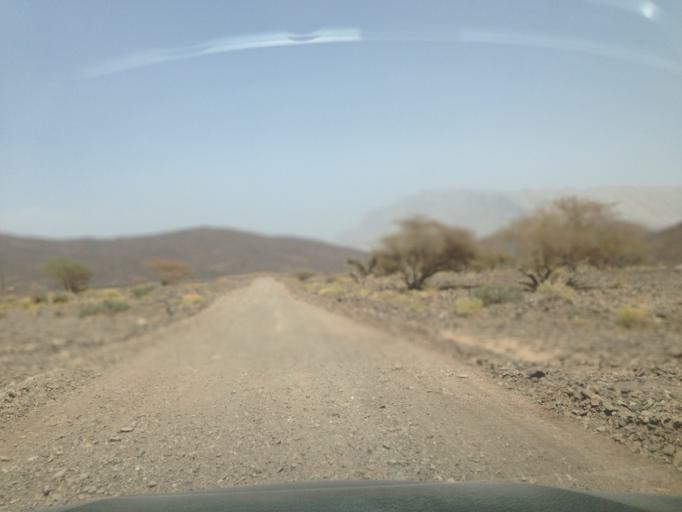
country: OM
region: Az Zahirah
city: `Ibri
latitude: 23.2008
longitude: 56.8693
